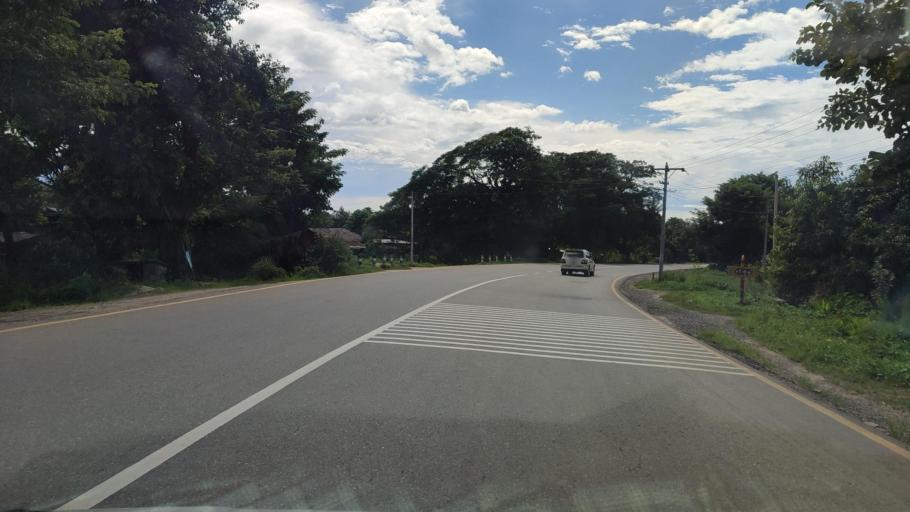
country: MM
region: Bago
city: Nyaunglebin
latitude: 18.1844
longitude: 96.5793
